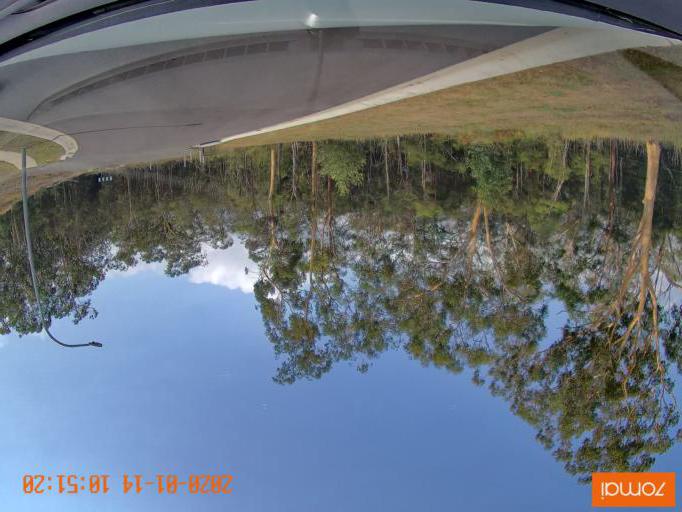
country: AU
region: New South Wales
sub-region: Lake Macquarie Shire
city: Dora Creek
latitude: -33.0985
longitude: 151.4839
